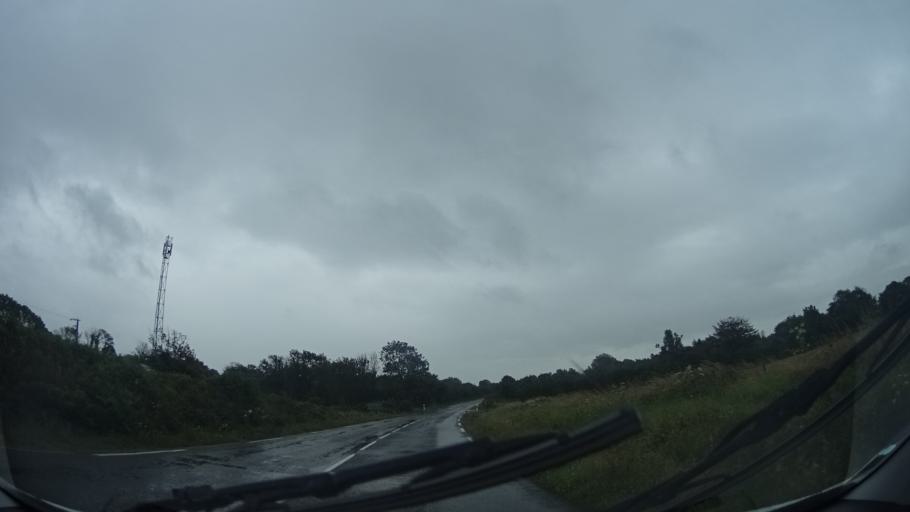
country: FR
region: Lower Normandy
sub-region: Departement de la Manche
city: Beaumont-Hague
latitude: 49.6047
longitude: -1.7839
